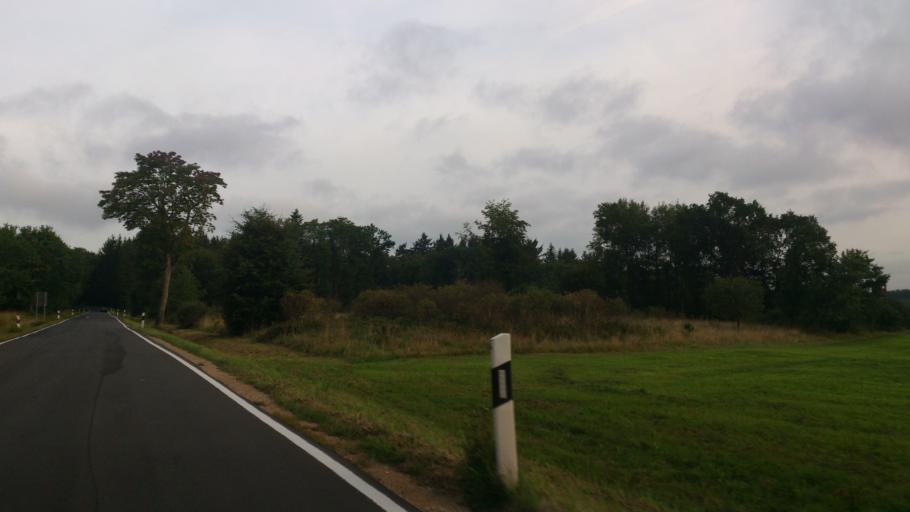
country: DE
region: Rheinland-Pfalz
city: Dankerath
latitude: 50.3076
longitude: 6.8056
